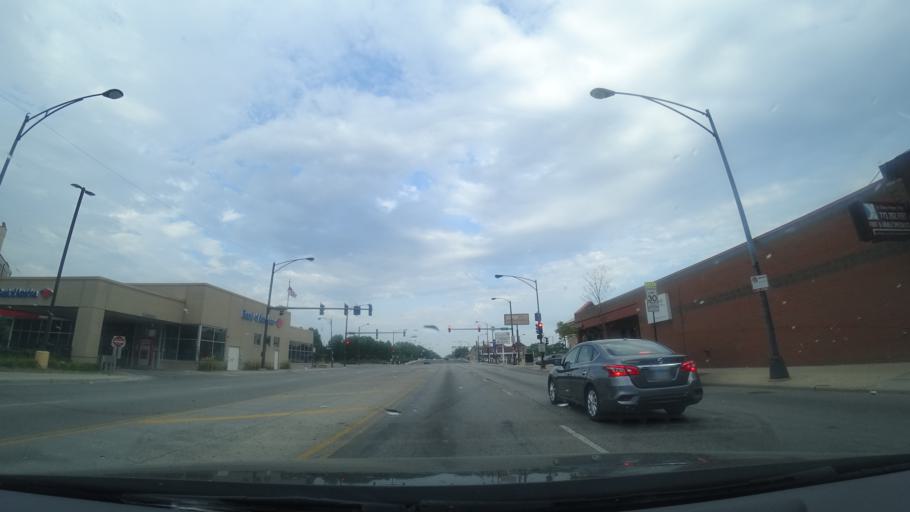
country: US
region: Illinois
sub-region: Cook County
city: Lincolnwood
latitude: 41.9905
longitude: -87.7060
